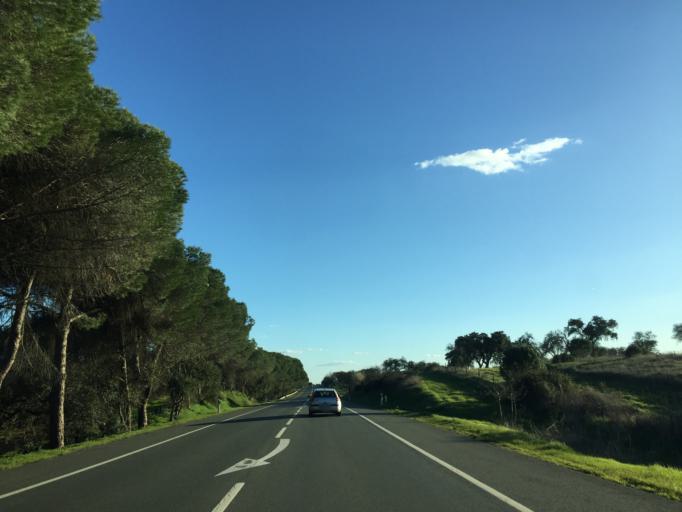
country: PT
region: Setubal
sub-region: Grandola
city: Grandola
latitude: 38.0842
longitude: -8.4175
